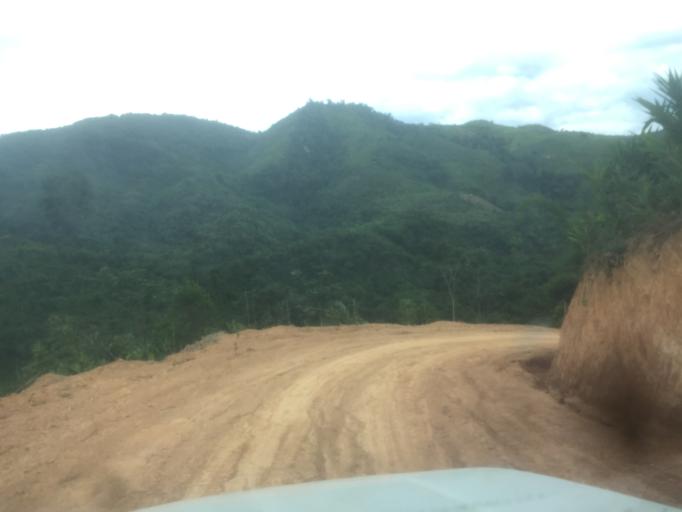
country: LA
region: Phongsali
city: Khoa
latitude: 20.9178
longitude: 102.5620
